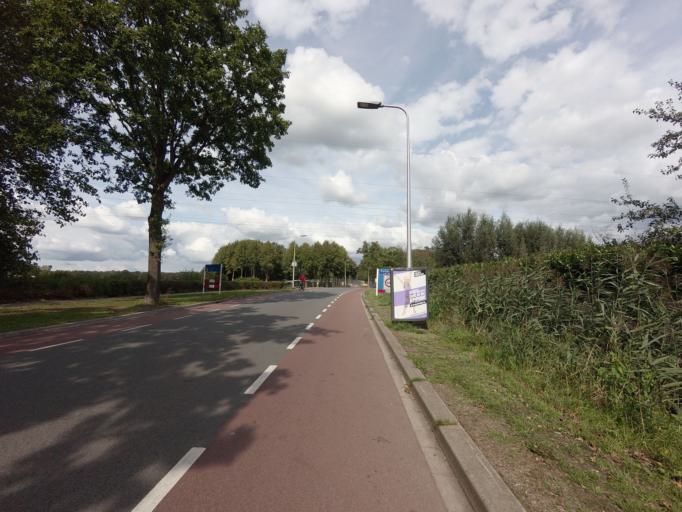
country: NL
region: Overijssel
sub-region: Gemeente Deventer
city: Schalkhaar
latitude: 52.2717
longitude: 6.1973
